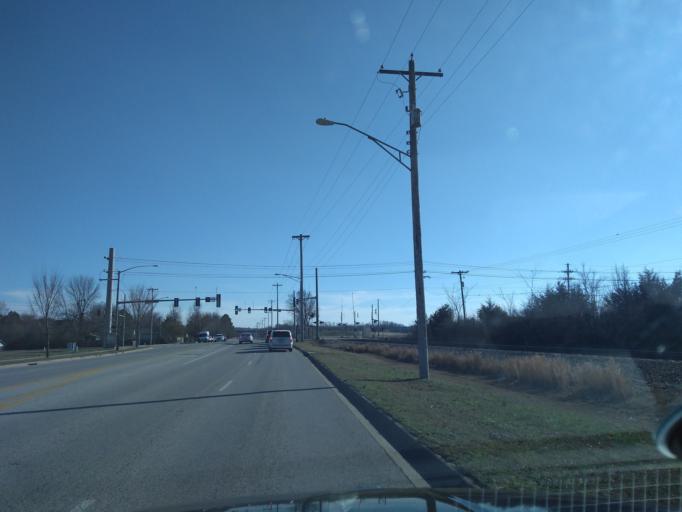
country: US
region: Arkansas
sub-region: Washington County
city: Johnson
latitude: 36.1179
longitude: -94.1635
